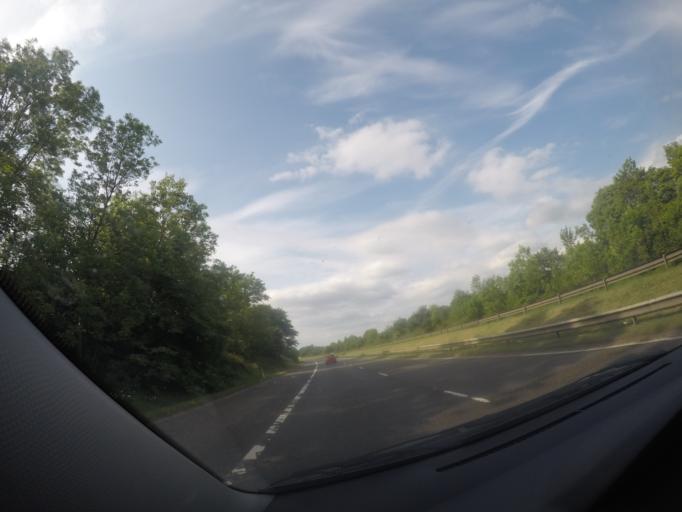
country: GB
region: Scotland
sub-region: South Lanarkshire
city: Larkhall
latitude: 55.7356
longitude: -3.9507
